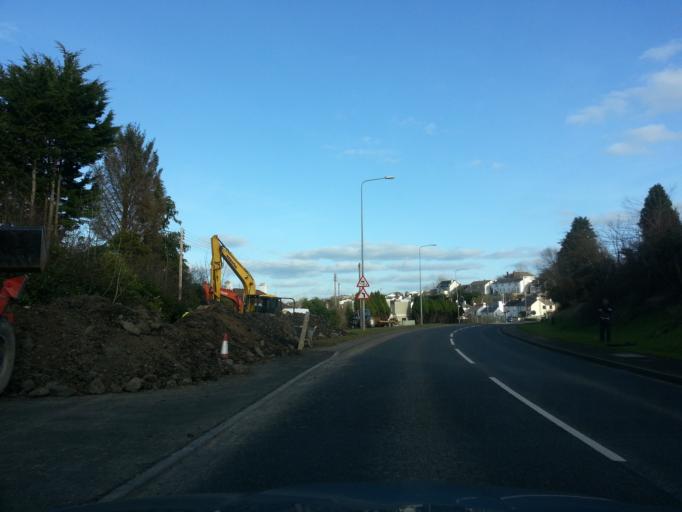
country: GB
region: Northern Ireland
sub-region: Fermanagh District
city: Enniskillen
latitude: 54.3366
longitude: -7.6555
